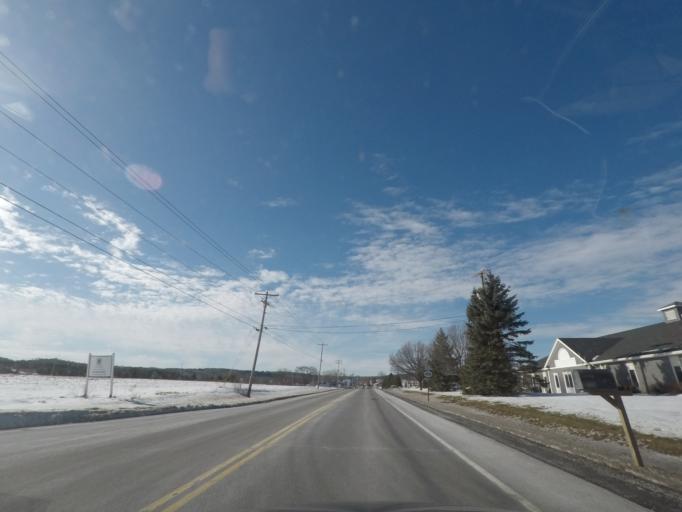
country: US
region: New York
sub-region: Albany County
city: Altamont
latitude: 42.7494
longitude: -74.0447
